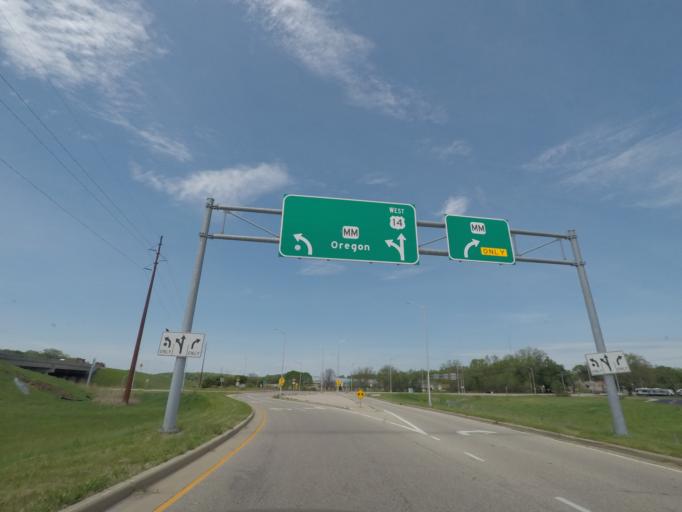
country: US
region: Wisconsin
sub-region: Dane County
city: Oregon
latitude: 42.9520
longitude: -89.3766
